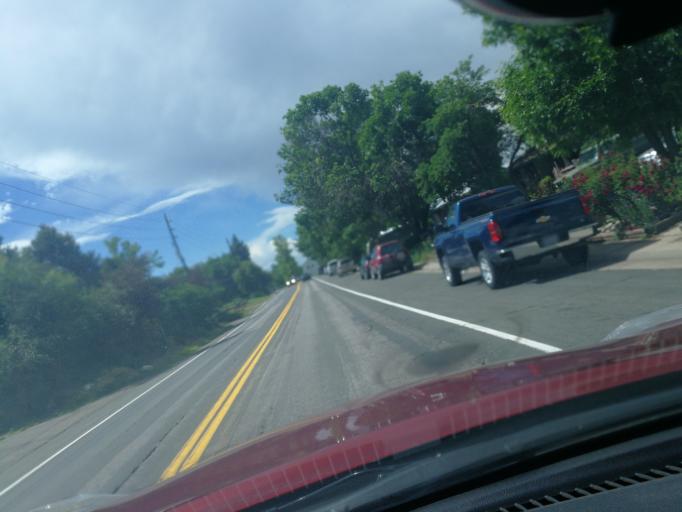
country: US
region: Colorado
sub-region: Arapahoe County
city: Littleton
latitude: 39.5926
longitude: -105.0009
